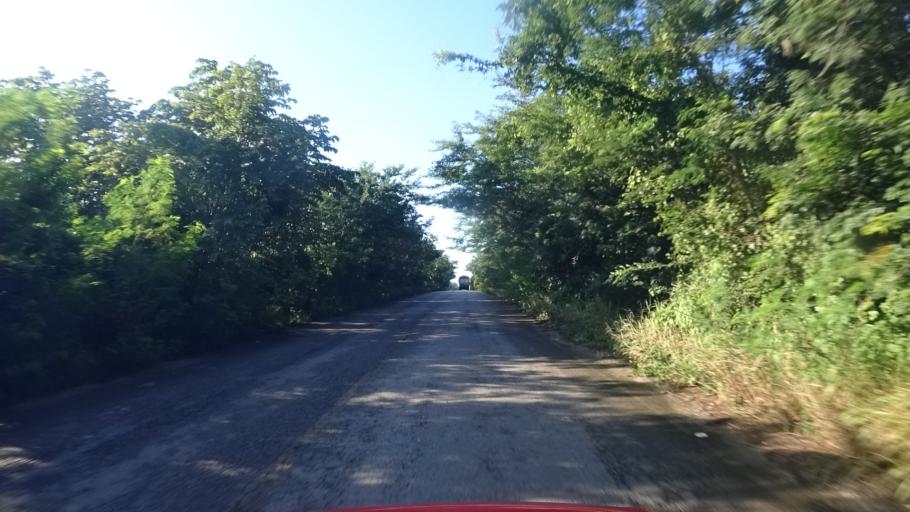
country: MX
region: Yucatan
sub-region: Tizimin
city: Tizimin
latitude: 21.1280
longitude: -88.1834
